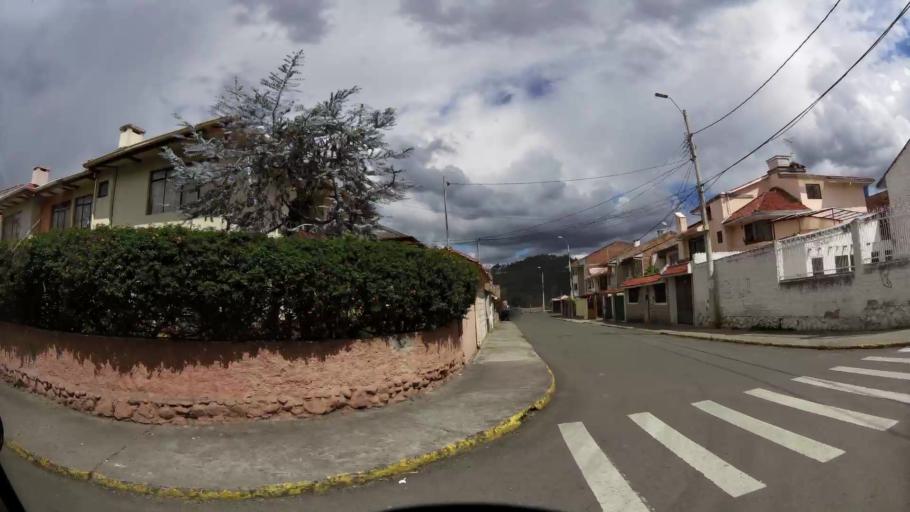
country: EC
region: Azuay
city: Cuenca
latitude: -2.9047
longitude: -78.9947
